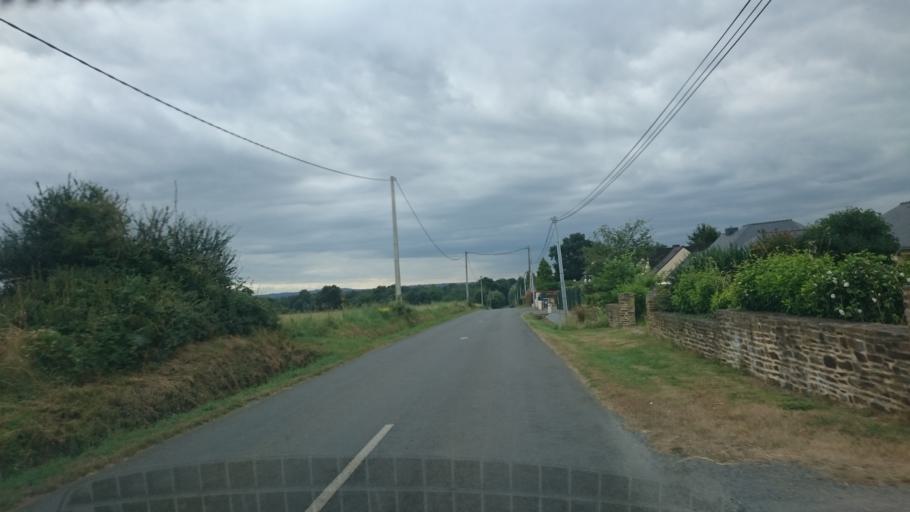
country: FR
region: Brittany
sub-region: Departement d'Ille-et-Vilaine
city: Meillac
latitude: 48.4142
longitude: -1.8404
